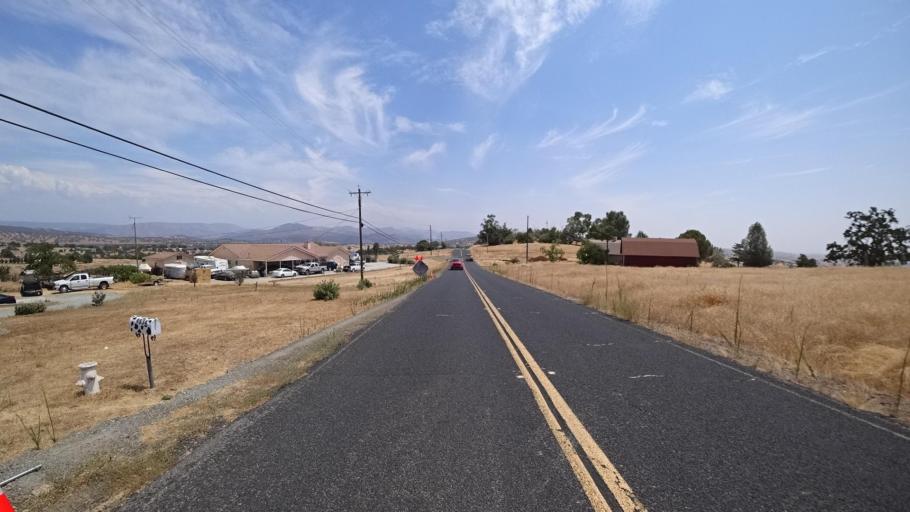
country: US
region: California
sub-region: Tuolumne County
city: Jamestown
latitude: 37.6541
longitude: -120.3456
